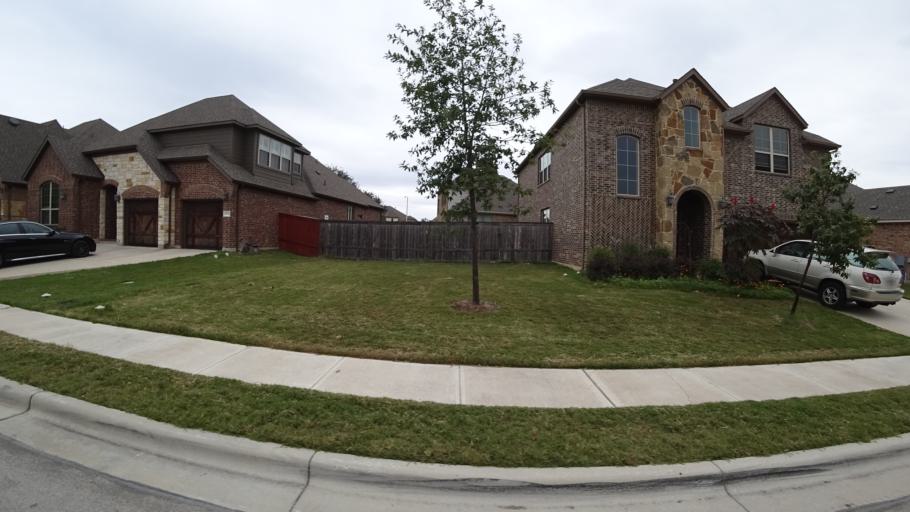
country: US
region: Texas
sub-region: Travis County
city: Manchaca
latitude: 30.1452
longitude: -97.8524
